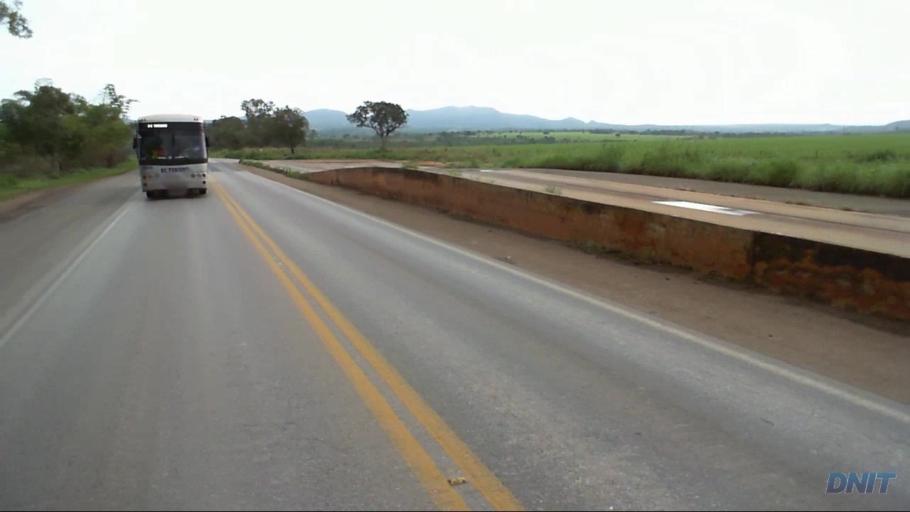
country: BR
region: Goias
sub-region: Uruacu
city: Uruacu
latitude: -14.6233
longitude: -49.1721
